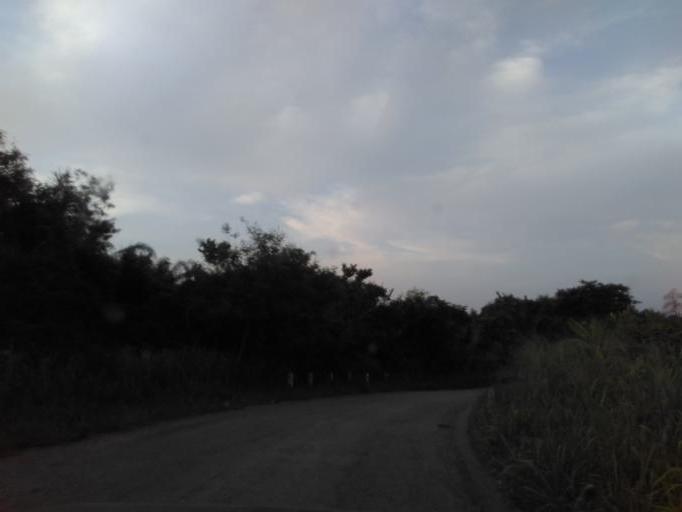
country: GH
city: Bekwai
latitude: 6.5495
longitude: -1.4373
